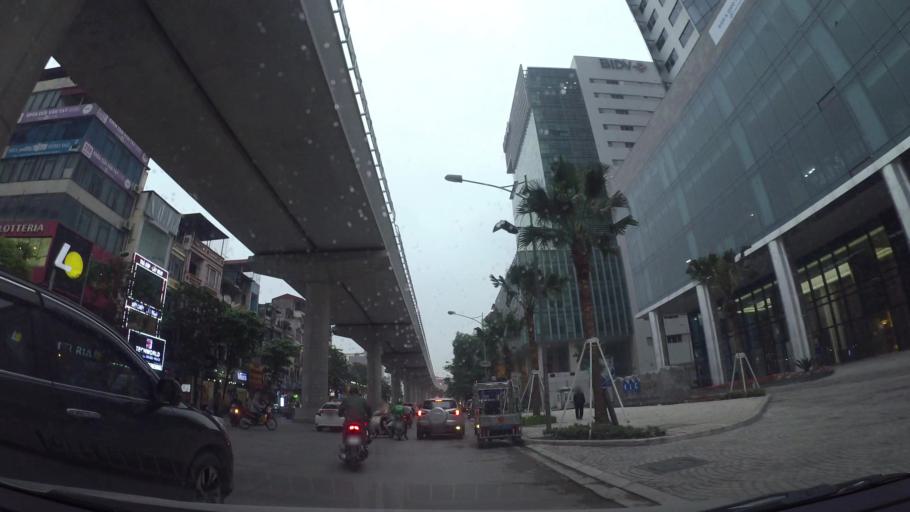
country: VN
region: Ha Noi
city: Cau Giay
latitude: 21.0349
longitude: 105.7947
